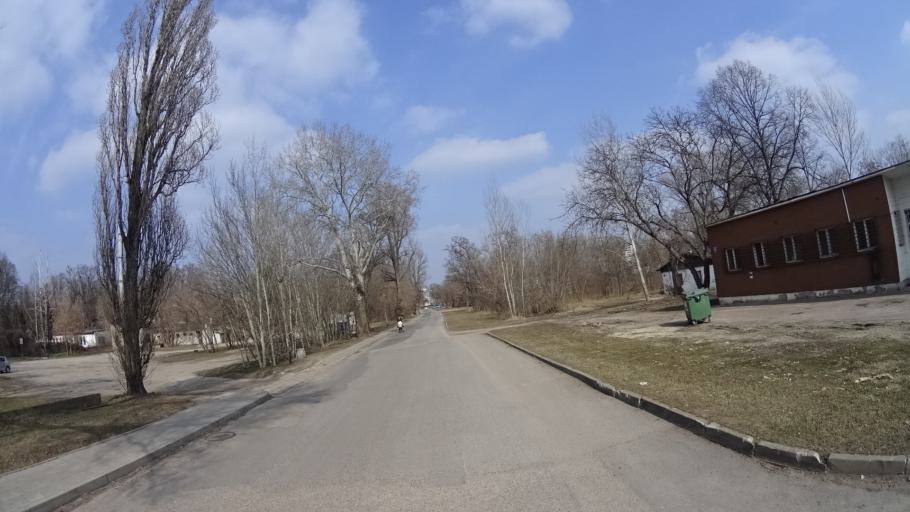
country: PL
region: Masovian Voivodeship
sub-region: Warszawa
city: Bielany
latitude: 52.2601
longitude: 20.9475
